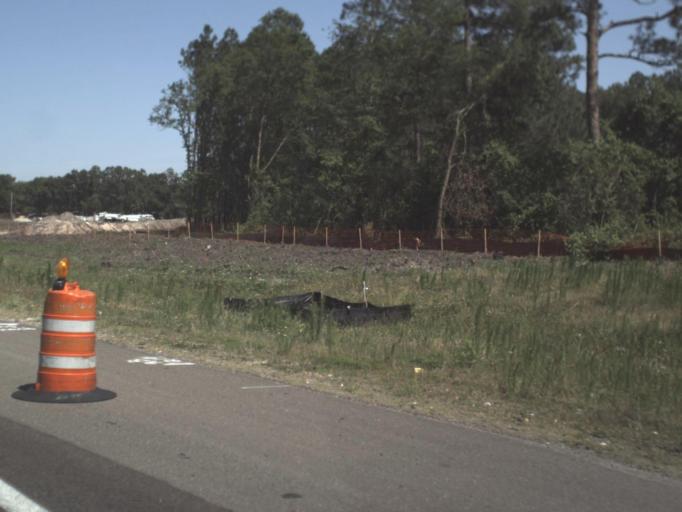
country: US
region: Florida
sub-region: Duval County
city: Jacksonville
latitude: 30.3146
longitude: -81.7969
